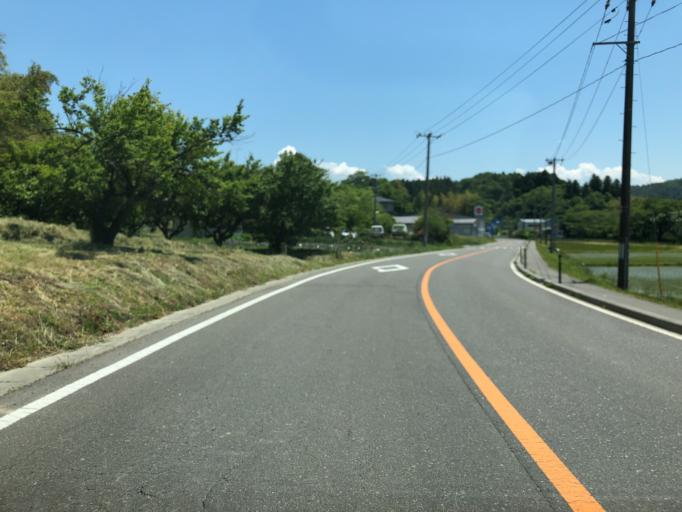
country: JP
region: Fukushima
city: Motomiya
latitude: 37.5002
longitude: 140.4628
